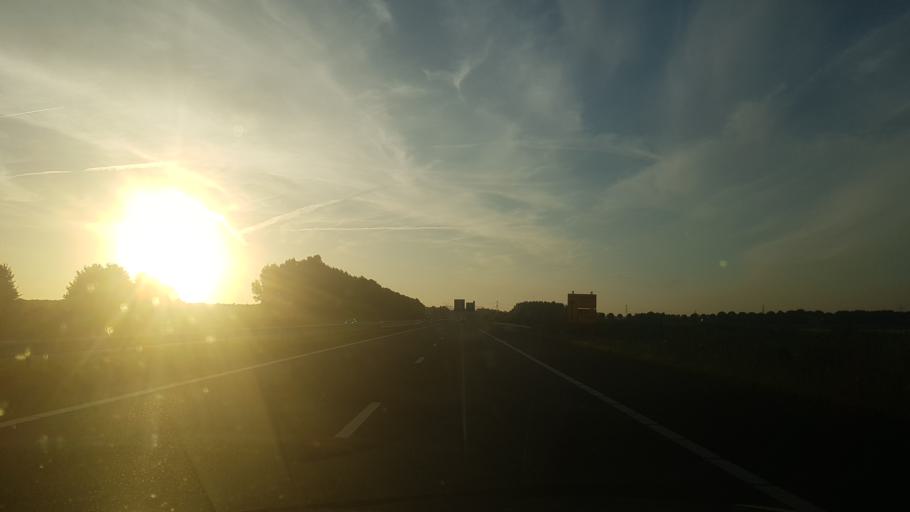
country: NL
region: Flevoland
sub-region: Gemeente Almere
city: Almere Stad
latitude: 52.3710
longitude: 5.3130
